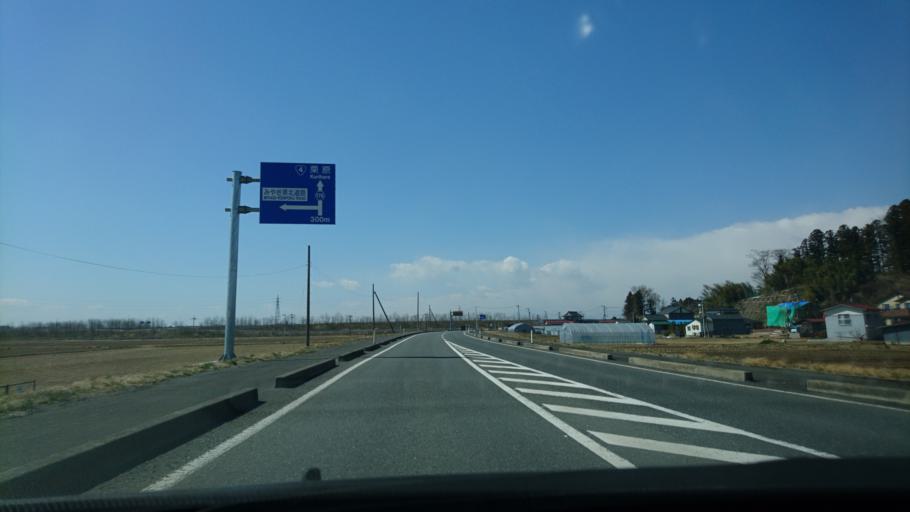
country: JP
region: Iwate
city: Ichinoseki
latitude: 38.7389
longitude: 141.1294
